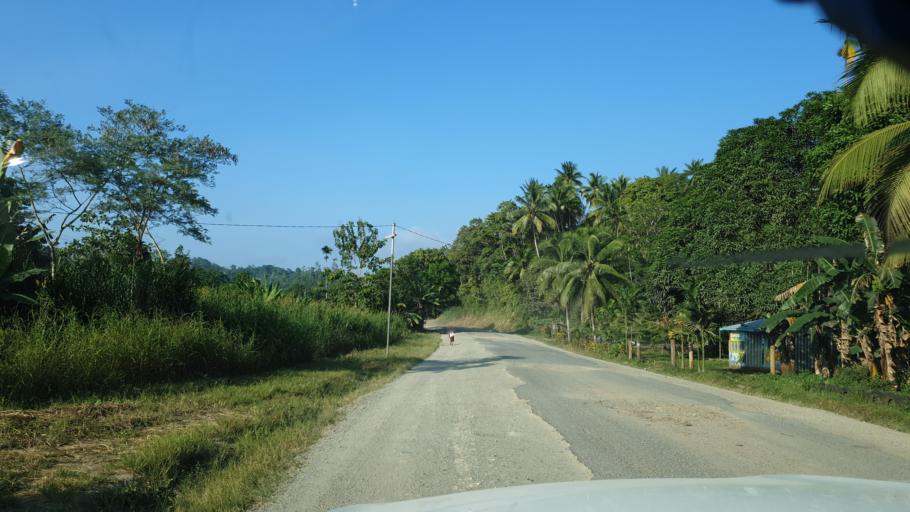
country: PG
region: East Sepik
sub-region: Wewak
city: Wewak
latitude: -3.6914
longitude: 143.6371
